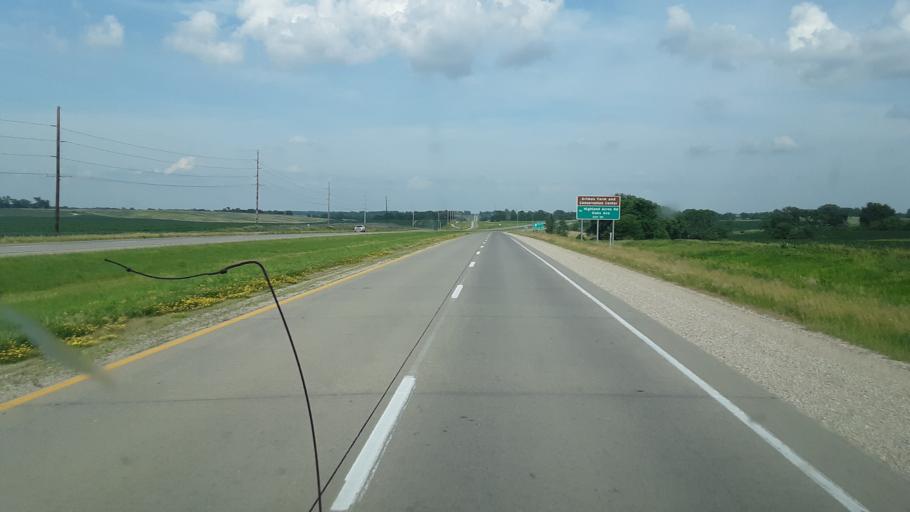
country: US
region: Iowa
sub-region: Marshall County
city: Marshalltown
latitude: 42.0074
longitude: -92.9919
